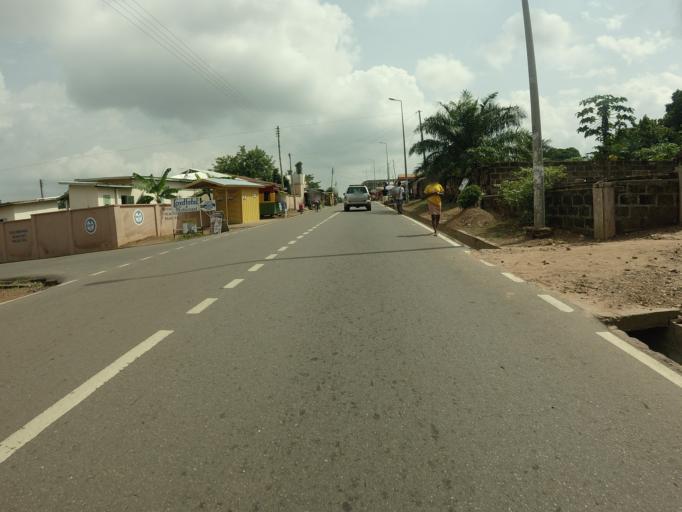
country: GH
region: Volta
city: Ho
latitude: 6.6189
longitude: 0.4746
